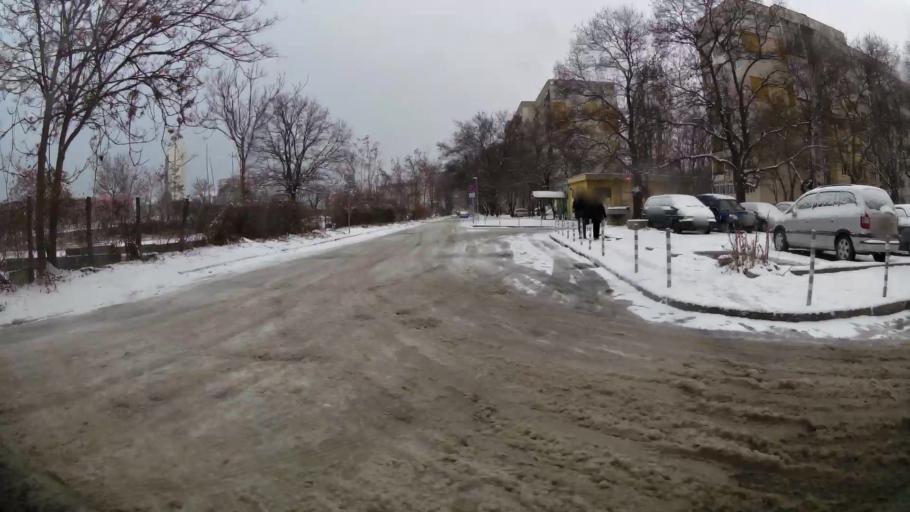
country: BG
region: Sofia-Capital
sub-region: Stolichna Obshtina
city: Sofia
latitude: 42.6967
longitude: 23.3052
